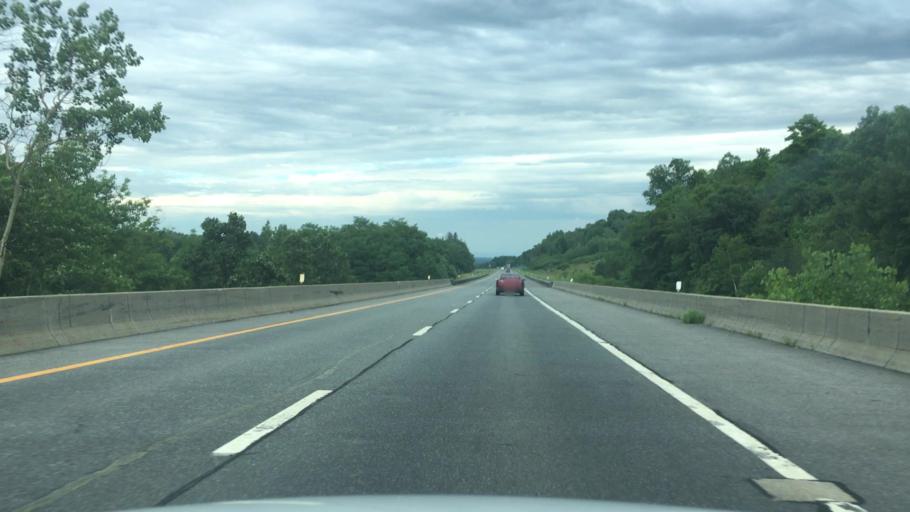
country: US
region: New York
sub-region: Albany County
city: Altamont
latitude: 42.7714
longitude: -74.0821
